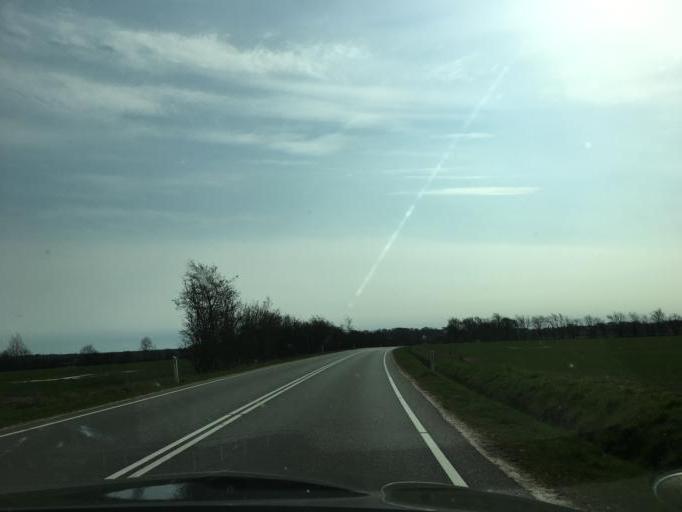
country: DK
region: South Denmark
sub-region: Vejen Kommune
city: Brorup
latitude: 55.4978
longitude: 9.0359
